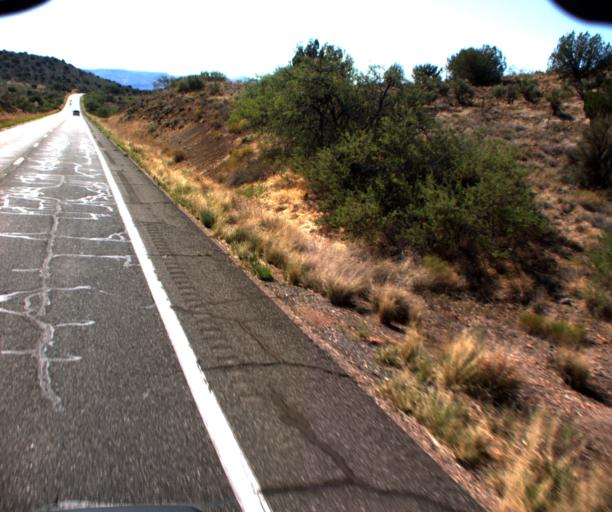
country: US
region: Arizona
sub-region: Yavapai County
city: Lake Montezuma
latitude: 34.6975
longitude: -111.7595
